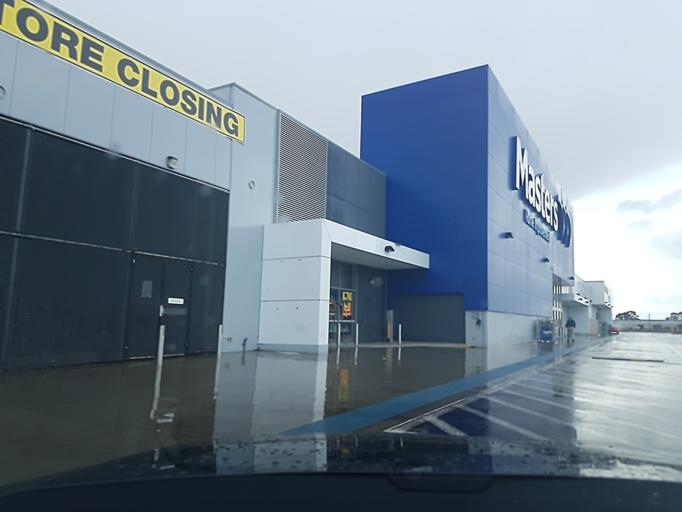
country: AU
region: Victoria
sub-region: Ballarat North
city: Newington
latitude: -37.5346
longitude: 143.8163
